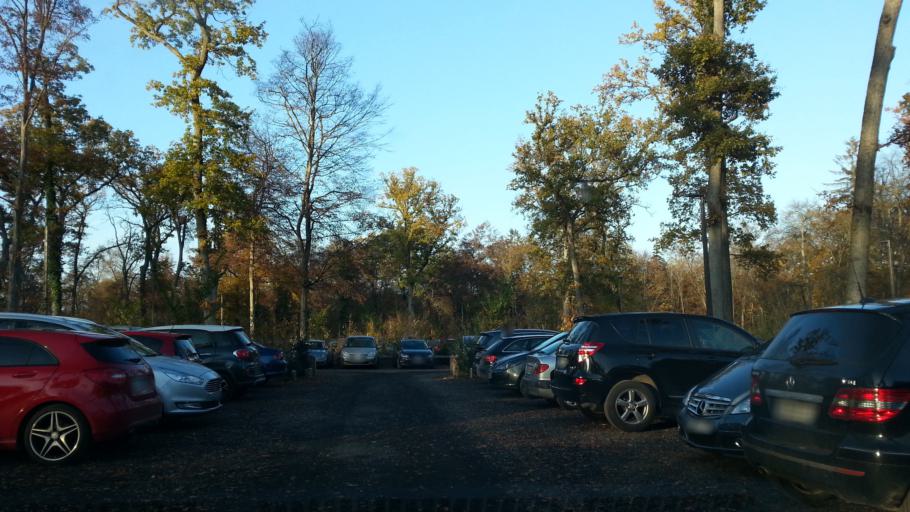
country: FR
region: Picardie
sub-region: Departement de l'Oise
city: Vineuil-Saint-Firmin
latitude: 49.1888
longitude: 2.4878
